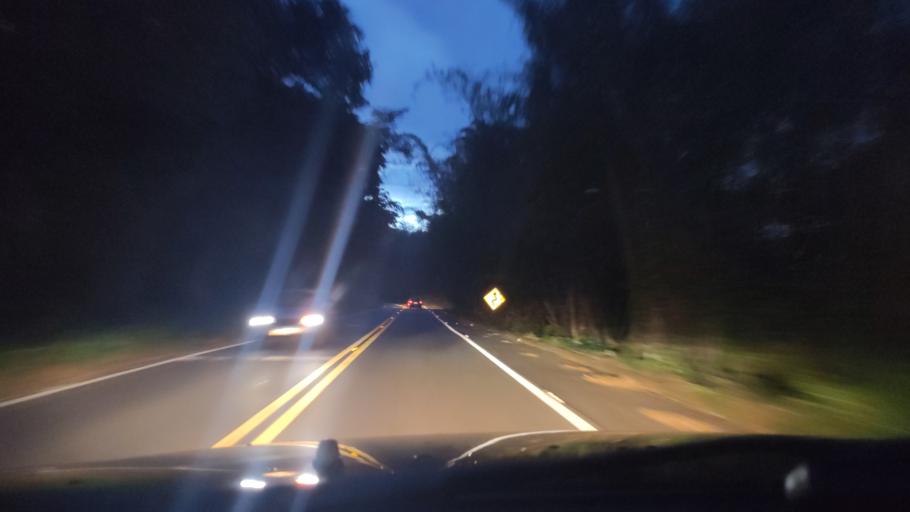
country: BR
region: Sao Paulo
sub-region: Socorro
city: Socorro
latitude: -22.5504
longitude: -46.5786
